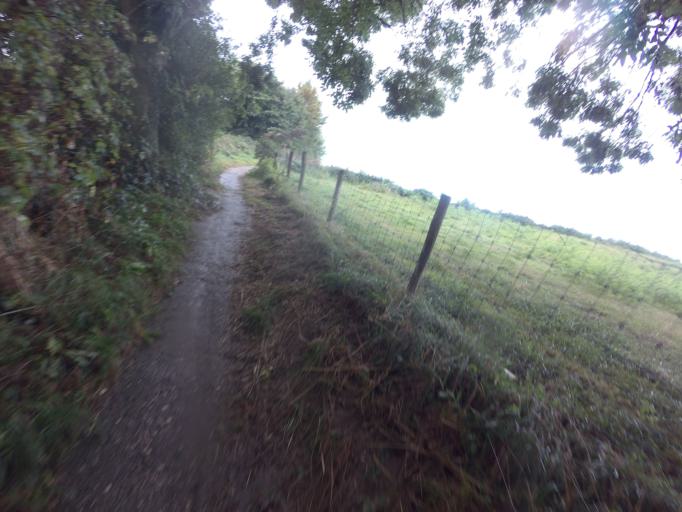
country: NL
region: Limburg
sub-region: Eijsden-Margraten
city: Margraten
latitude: 50.7906
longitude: 5.8008
